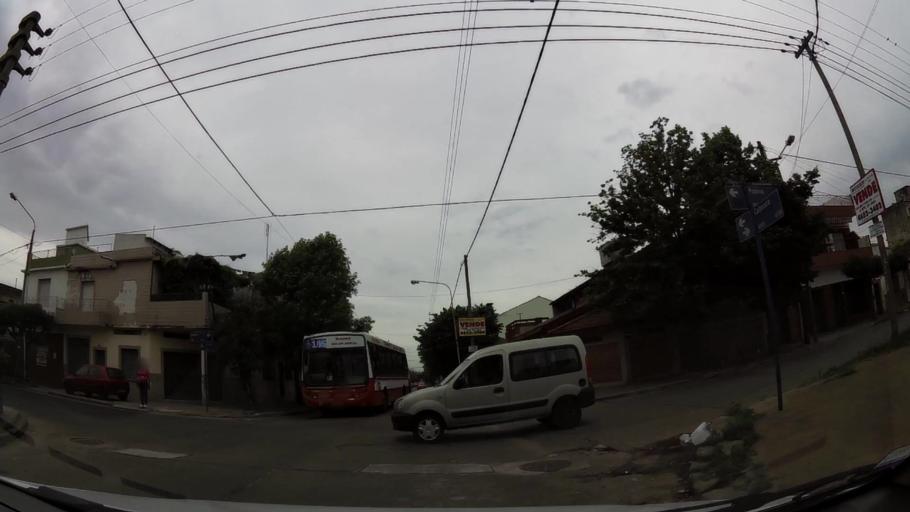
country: AR
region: Buenos Aires
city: San Justo
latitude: -34.6765
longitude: -58.5183
